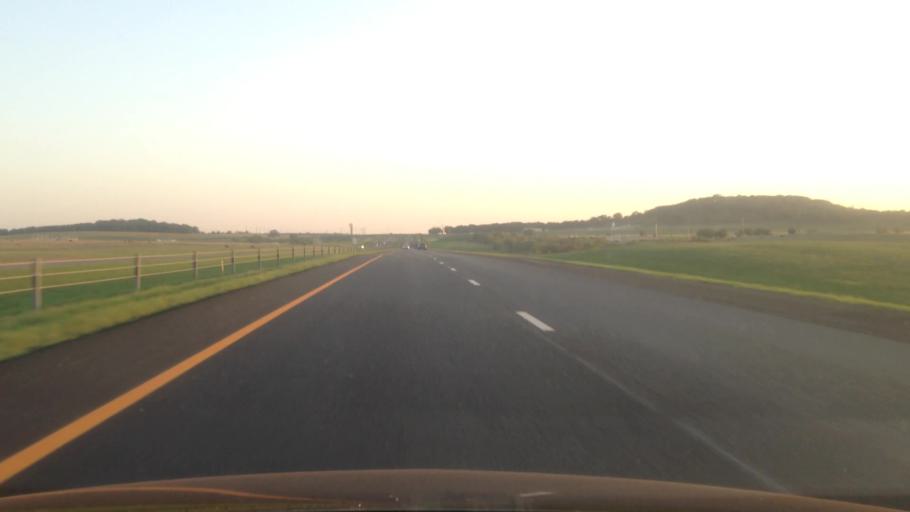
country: US
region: Texas
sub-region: Denton County
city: Argyle
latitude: 33.1605
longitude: -97.1880
